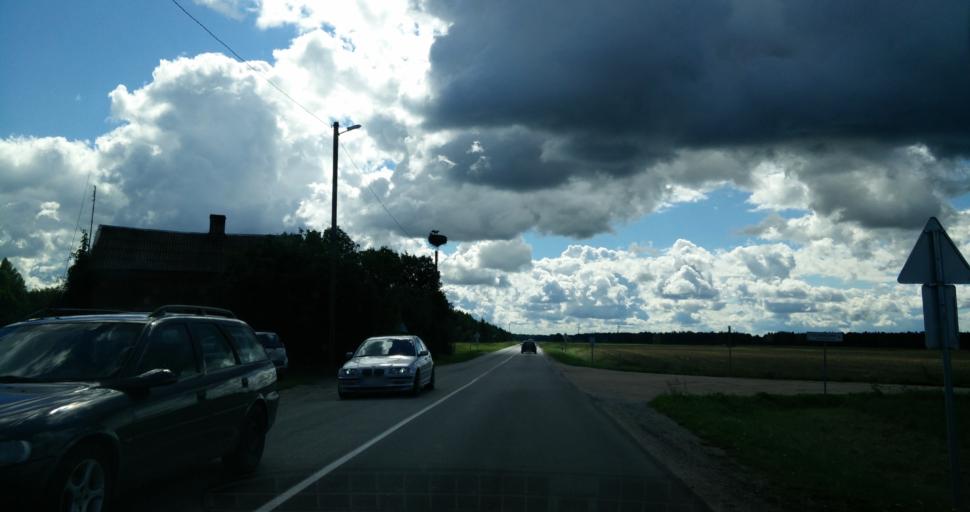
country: LT
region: Klaipedos apskritis
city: Silute
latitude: 55.3261
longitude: 21.5243
